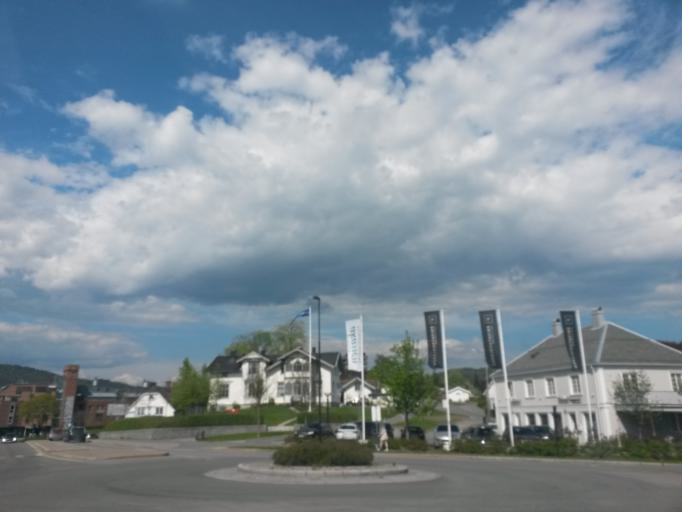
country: NO
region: Akershus
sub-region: Asker
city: Asker
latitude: 59.8343
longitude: 10.4372
